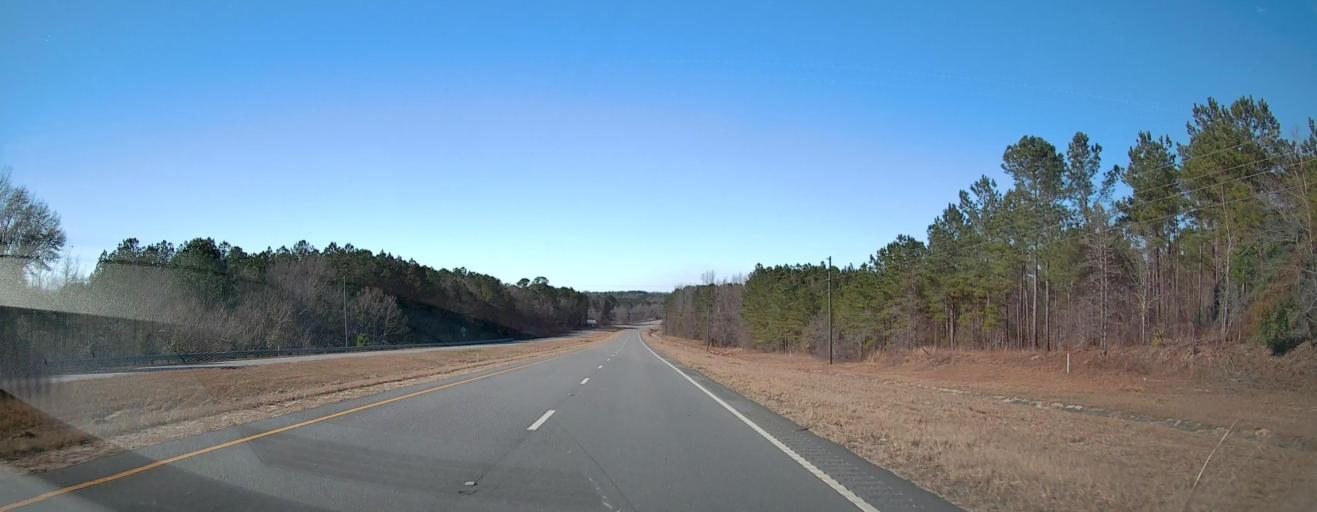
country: US
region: Georgia
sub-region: Taylor County
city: Butler
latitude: 32.6134
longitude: -84.2403
